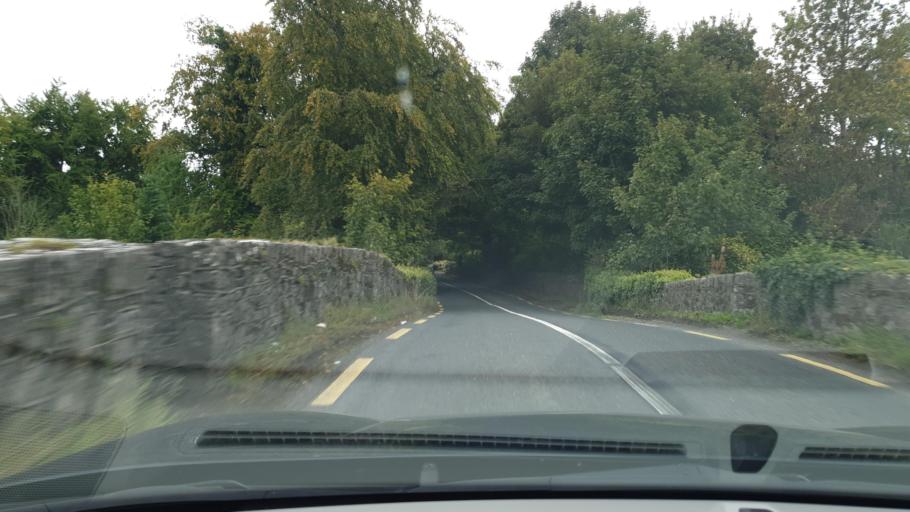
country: IE
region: Leinster
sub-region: Kildare
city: Sallins
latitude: 53.2641
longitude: -6.6803
